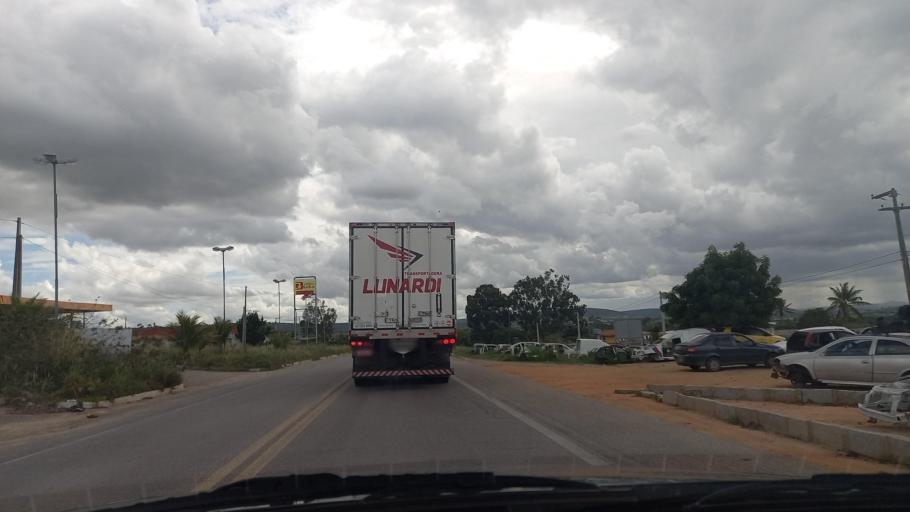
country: BR
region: Pernambuco
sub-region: Lajedo
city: Lajedo
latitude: -8.6608
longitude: -36.3412
